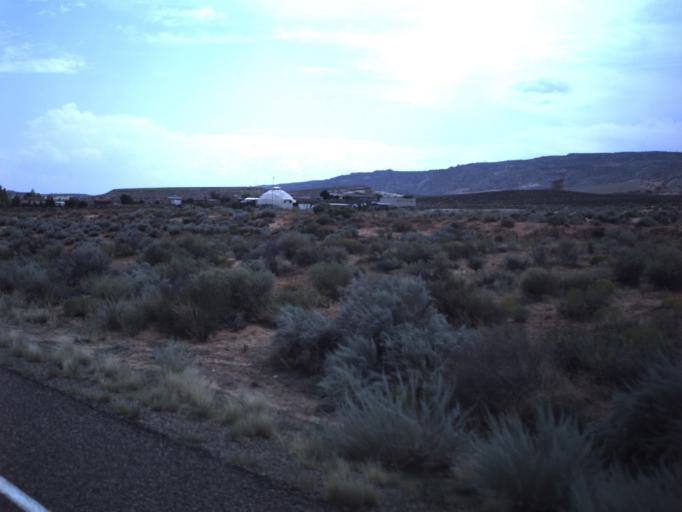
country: US
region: Arizona
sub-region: Coconino County
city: Page
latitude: 37.0694
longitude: -111.6493
